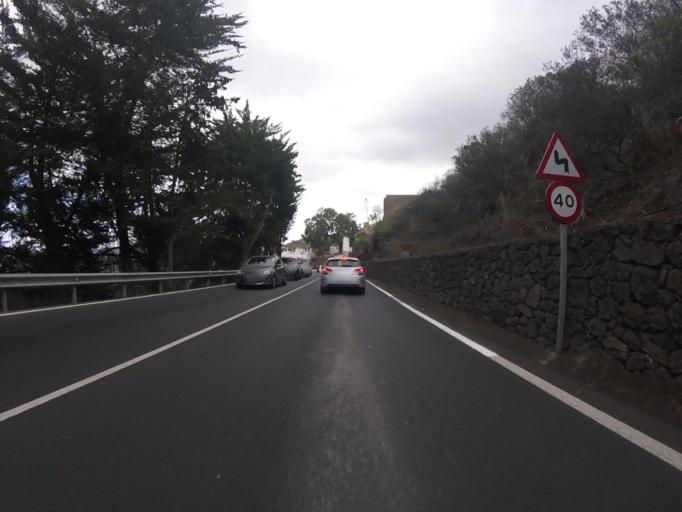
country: ES
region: Canary Islands
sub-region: Provincia de Las Palmas
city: Vega de San Mateo
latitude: 28.0175
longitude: -15.5232
